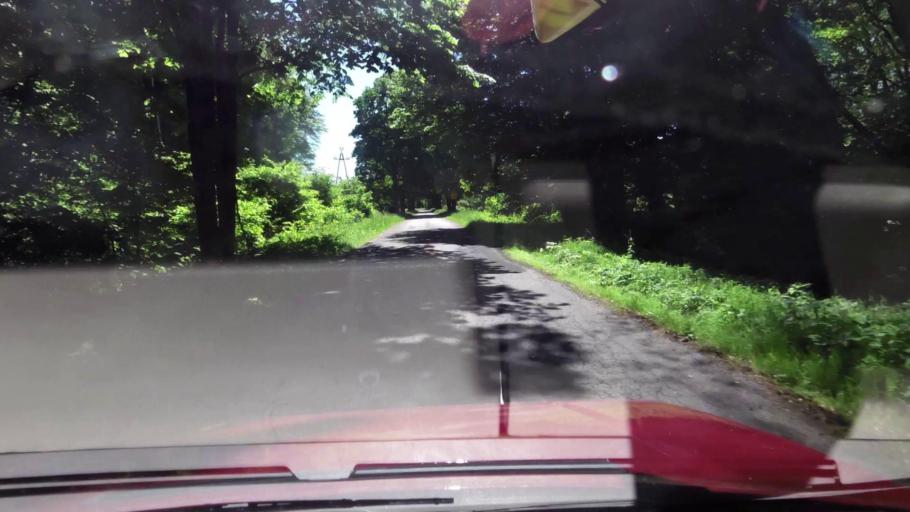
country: PL
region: West Pomeranian Voivodeship
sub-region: Powiat koszalinski
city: Bobolice
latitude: 54.0253
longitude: 16.6411
